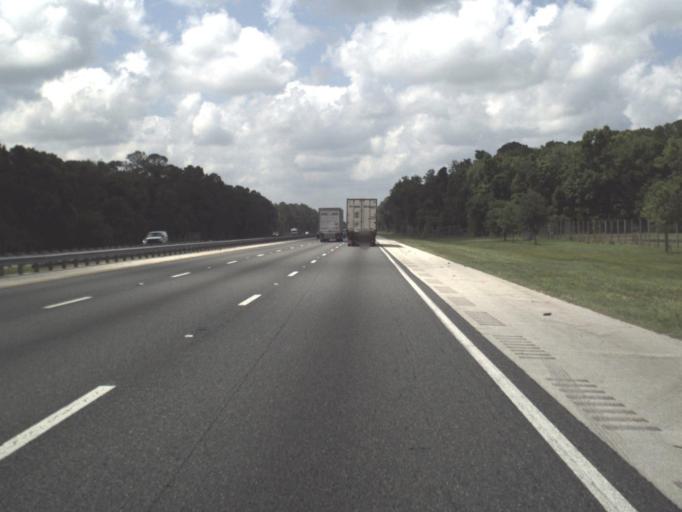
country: US
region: Florida
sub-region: Saint Johns County
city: Saint Augustine South
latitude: 29.8675
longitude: -81.3967
